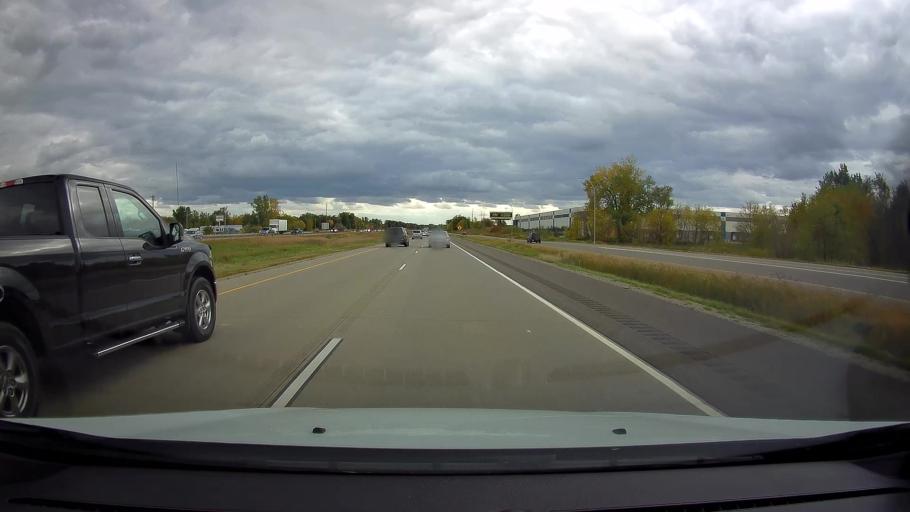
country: US
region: Minnesota
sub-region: Anoka County
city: Centerville
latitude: 45.1584
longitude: -93.0316
